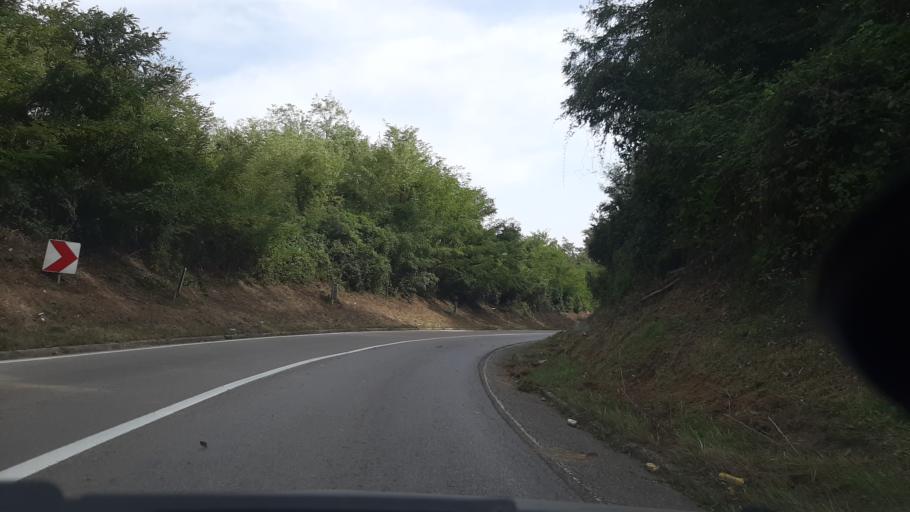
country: BA
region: Republika Srpska
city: Laktasi
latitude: 44.8741
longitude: 17.3577
